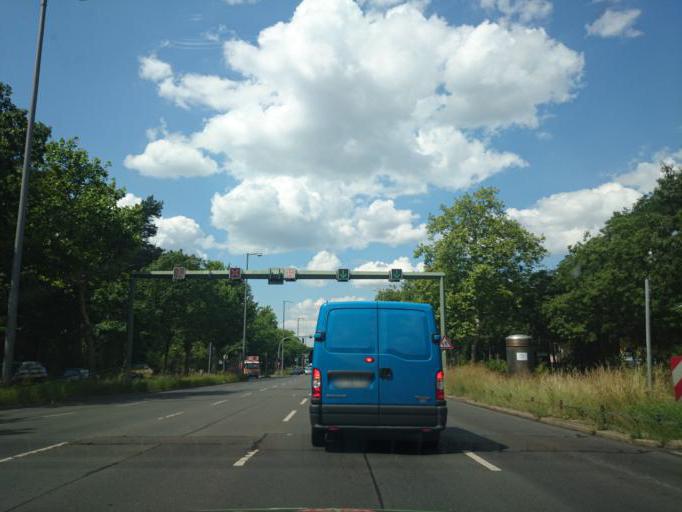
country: DE
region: Berlin
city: Haselhorst
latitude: 52.5086
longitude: 13.2194
